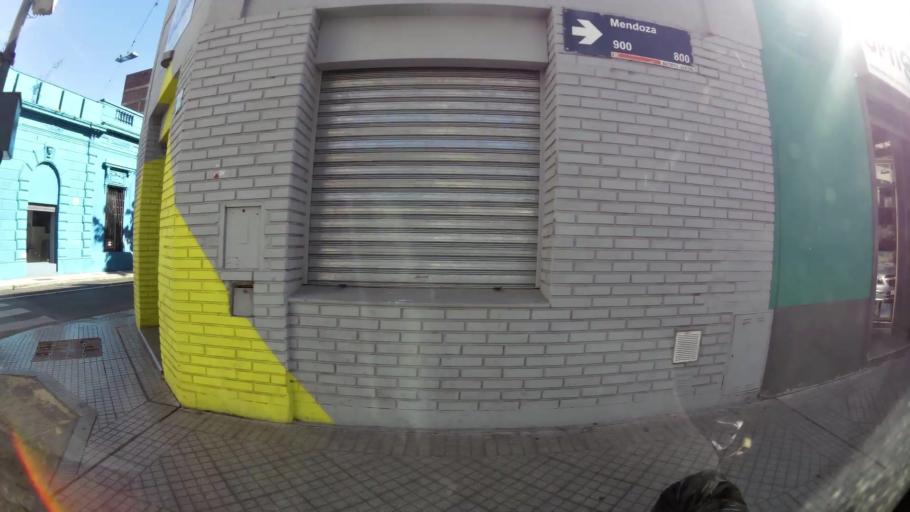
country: AR
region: Santa Fe
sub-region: Departamento de Rosario
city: Rosario
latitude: -32.9520
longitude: -60.6364
